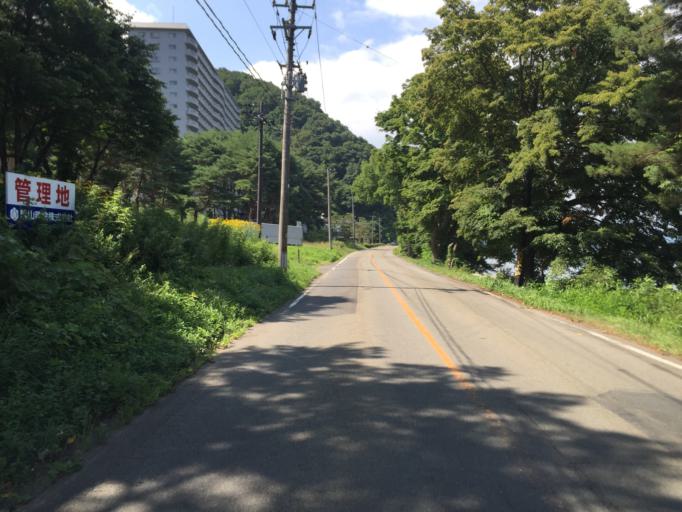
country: JP
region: Fukushima
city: Inawashiro
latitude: 37.4614
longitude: 140.1549
